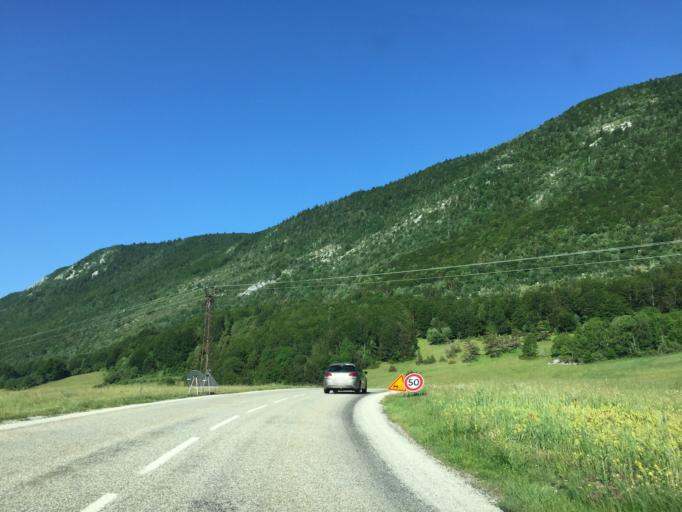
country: FR
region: Rhone-Alpes
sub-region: Departement de la Drome
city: Saint-Laurent-en-Royans
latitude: 44.9281
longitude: 5.3825
